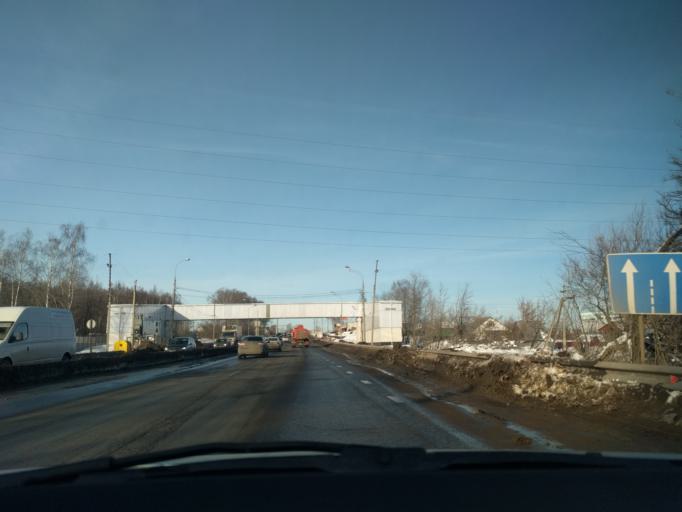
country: RU
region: Moskovskaya
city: Sheremet'yevskiy
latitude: 56.0015
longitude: 37.5386
